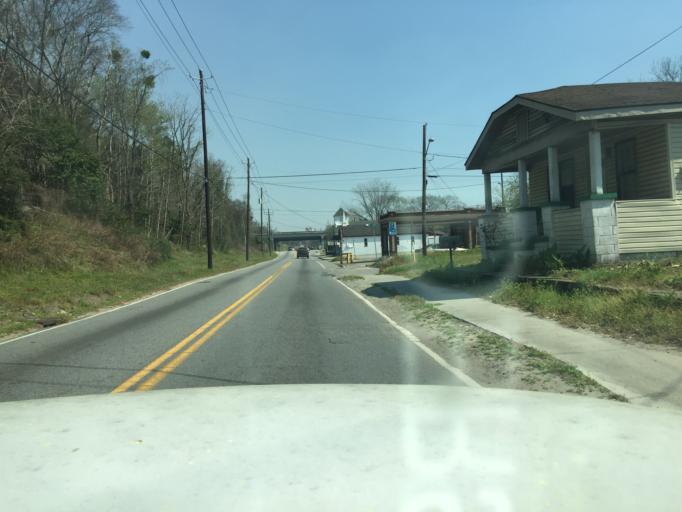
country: US
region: Georgia
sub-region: Chatham County
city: Savannah
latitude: 32.0788
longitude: -81.1101
